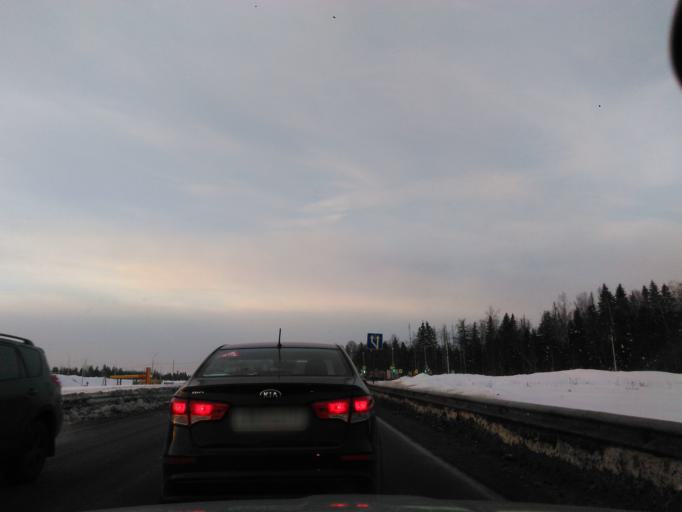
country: RU
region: Moskovskaya
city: Povarovo
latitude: 56.0082
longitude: 37.0258
